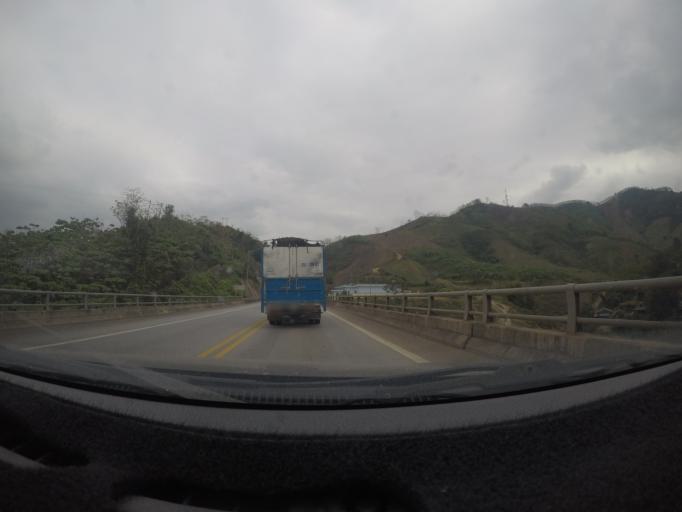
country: VN
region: Lao Cai
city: Thi Tran Pho Rang
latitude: 22.0965
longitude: 104.4264
